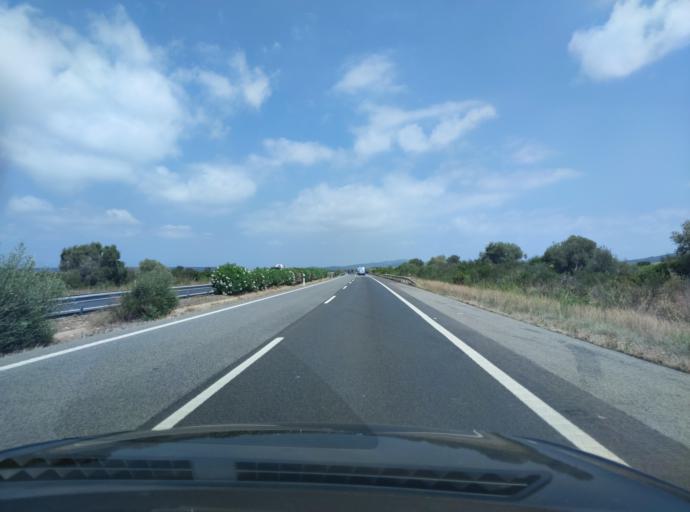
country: ES
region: Catalonia
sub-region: Provincia de Tarragona
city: Alcanar
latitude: 40.5334
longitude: 0.4188
